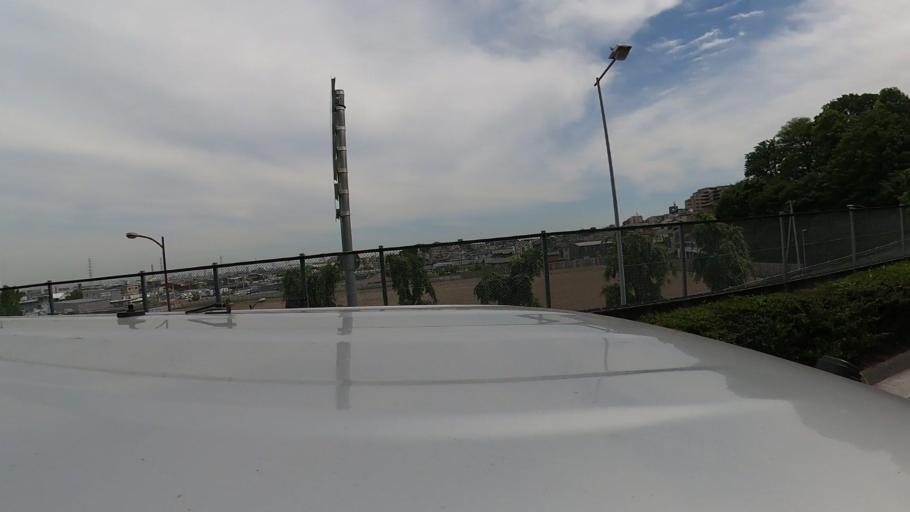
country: JP
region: Saitama
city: Wako
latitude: 35.8002
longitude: 139.6192
